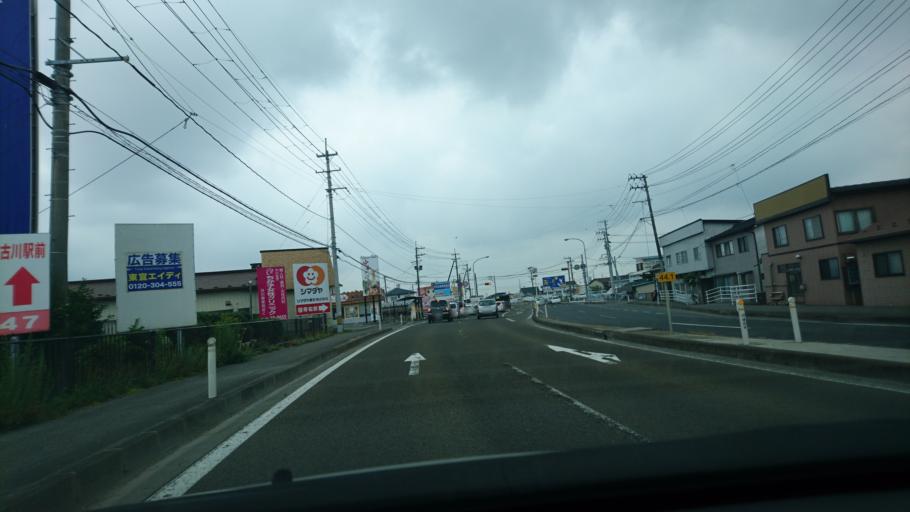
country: JP
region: Miyagi
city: Furukawa
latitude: 38.5907
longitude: 140.9391
